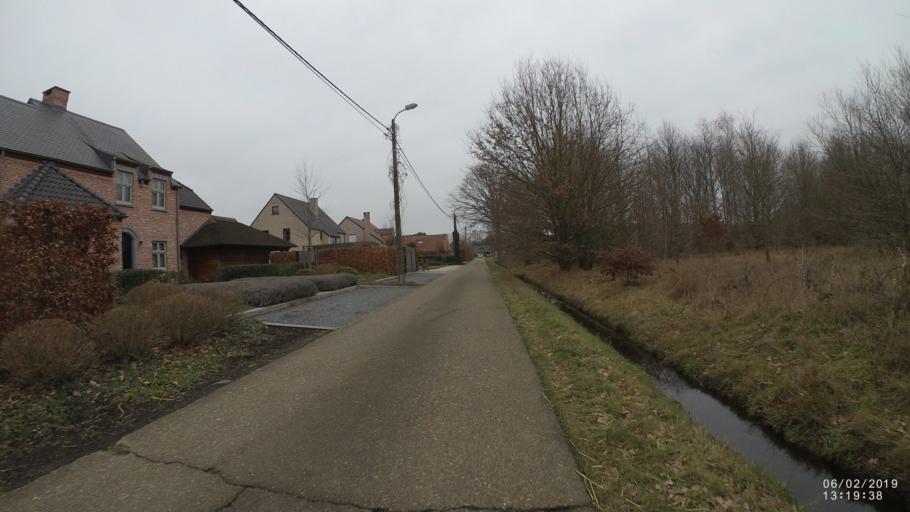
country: BE
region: Flanders
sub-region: Provincie Vlaams-Brabant
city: Begijnendijk
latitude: 51.0234
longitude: 4.8116
